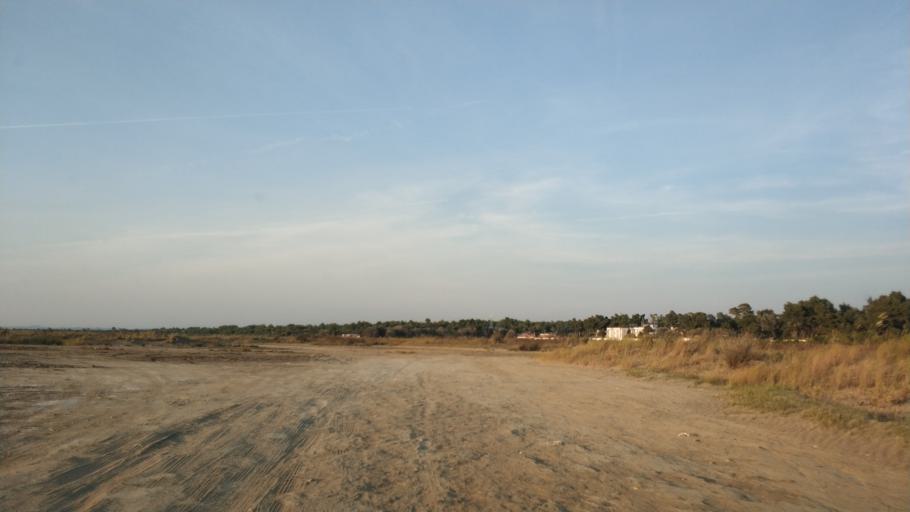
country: AL
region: Fier
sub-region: Rrethi i Lushnjes
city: Divjake
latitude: 40.9674
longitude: 19.4756
